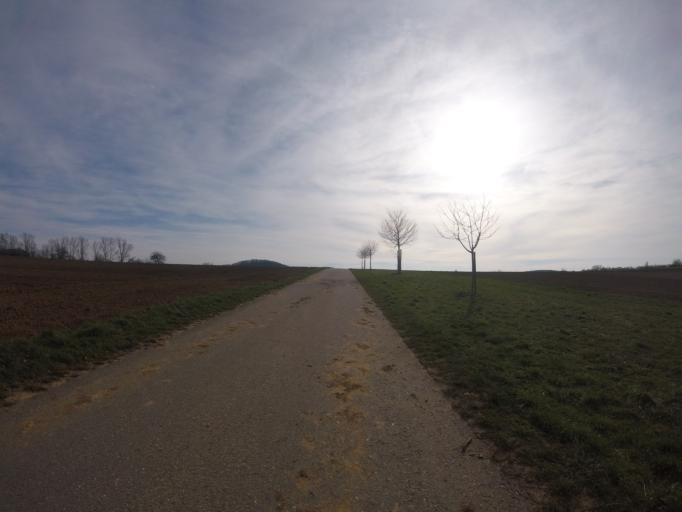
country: DE
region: Baden-Wuerttemberg
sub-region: Regierungsbezirk Stuttgart
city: Abstatt
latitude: 49.0473
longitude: 9.2862
